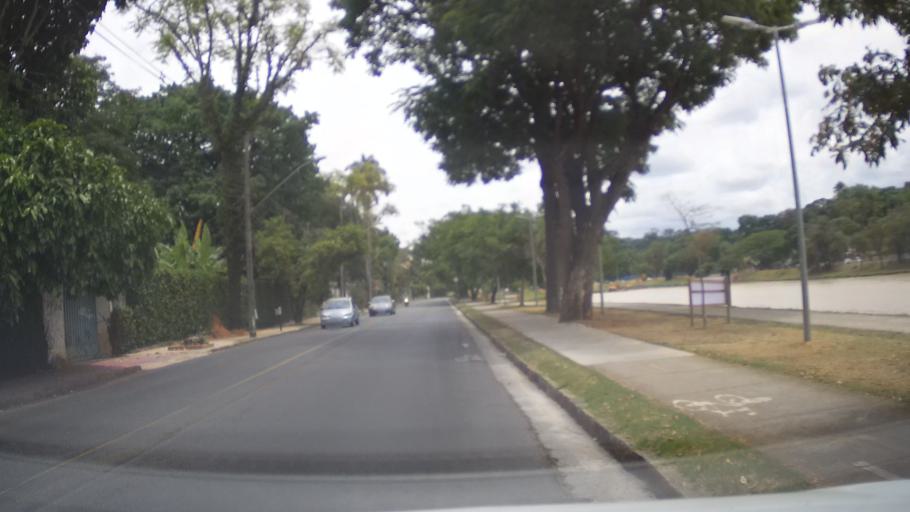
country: BR
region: Minas Gerais
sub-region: Belo Horizonte
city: Belo Horizonte
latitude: -19.8480
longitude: -43.9962
